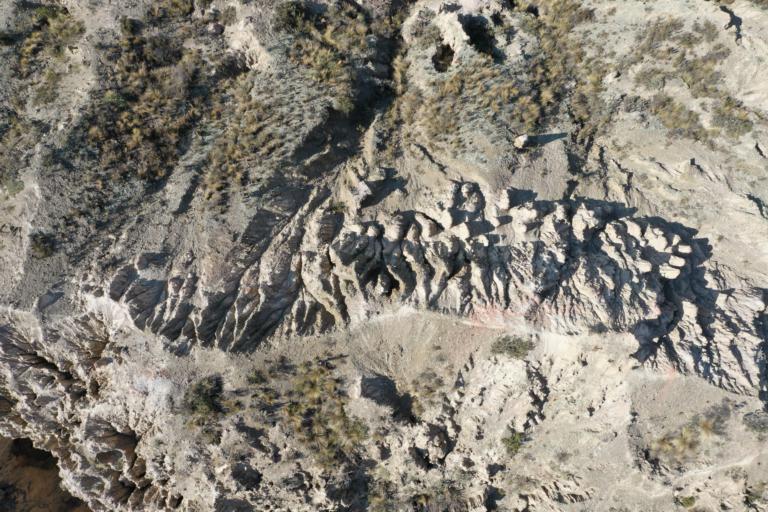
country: BO
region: La Paz
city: La Paz
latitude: -16.5604
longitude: -68.1225
